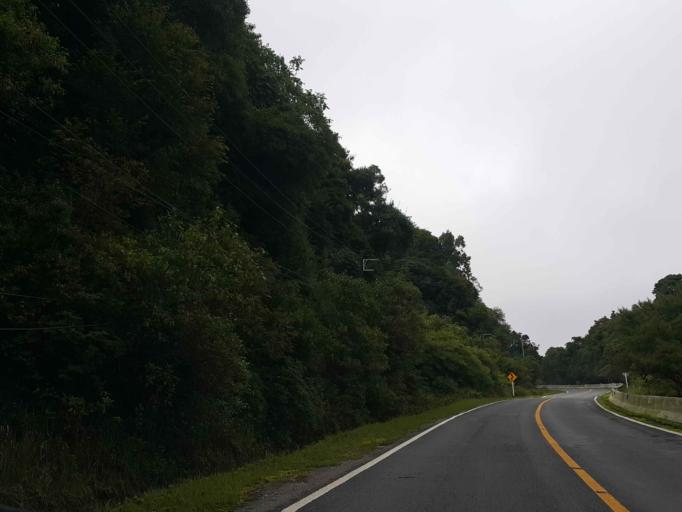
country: TH
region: Chiang Mai
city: Mae Chaem
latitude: 18.5721
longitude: 98.4835
